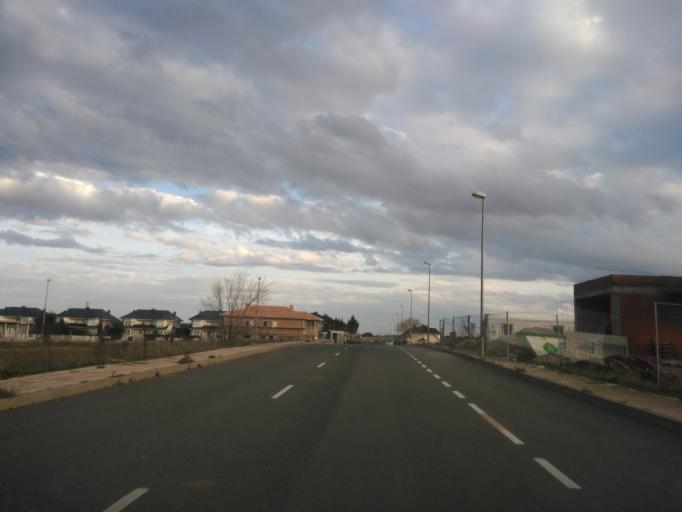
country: ES
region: Castille and Leon
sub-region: Provincia de Salamanca
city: Santa Marta de Tormes
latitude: 40.9300
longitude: -5.6290
